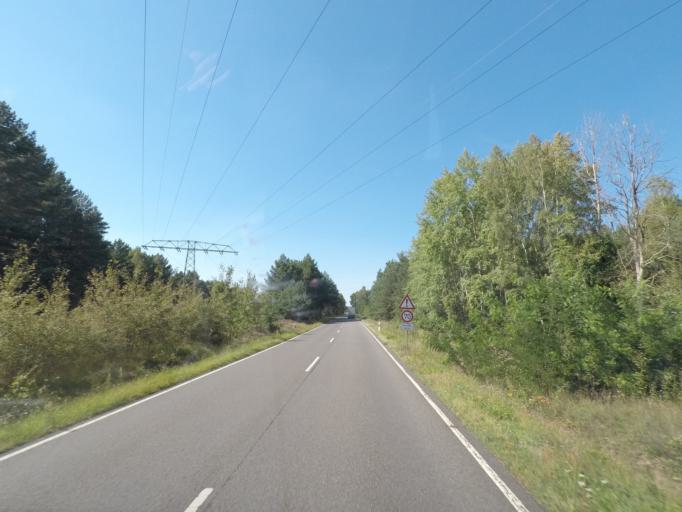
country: DE
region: Brandenburg
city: Welzow
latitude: 51.5666
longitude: 14.1075
